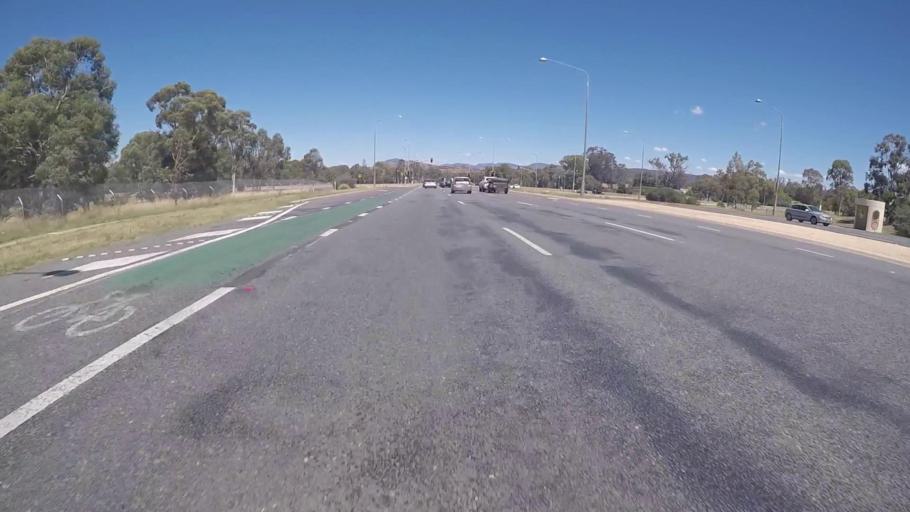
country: AU
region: Australian Capital Territory
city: Macarthur
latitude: -35.3729
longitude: 149.0573
